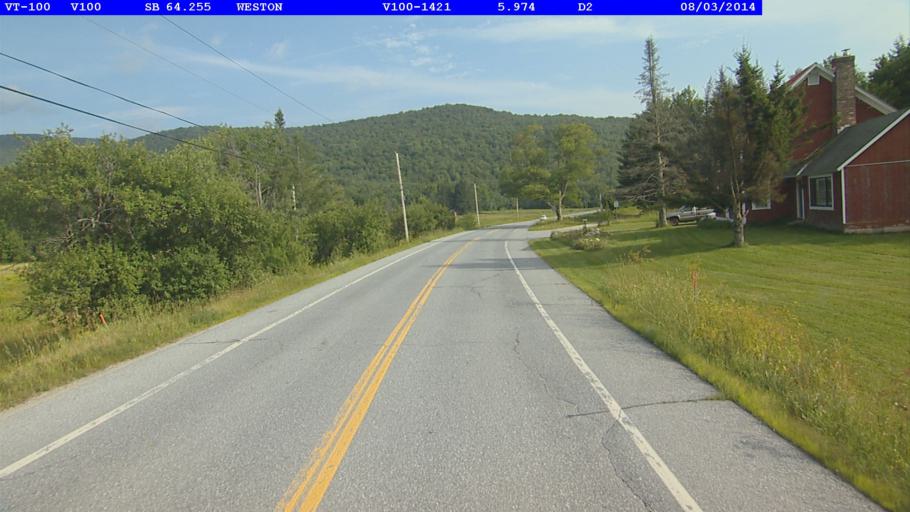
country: US
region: Vermont
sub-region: Windsor County
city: Chester
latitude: 43.3291
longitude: -72.7814
